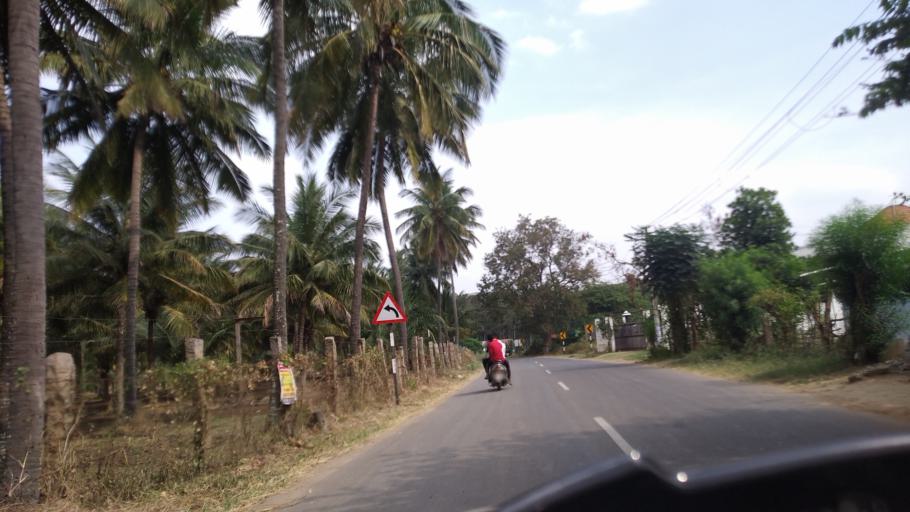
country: IN
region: Tamil Nadu
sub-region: Coimbatore
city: Perur
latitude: 10.9623
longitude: 76.7463
